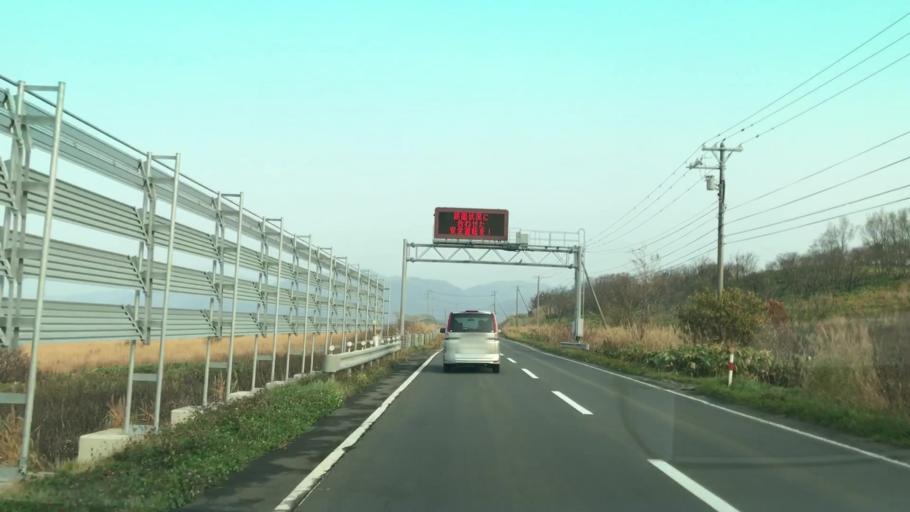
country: JP
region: Hokkaido
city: Ishikari
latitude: 43.3771
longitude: 141.4283
